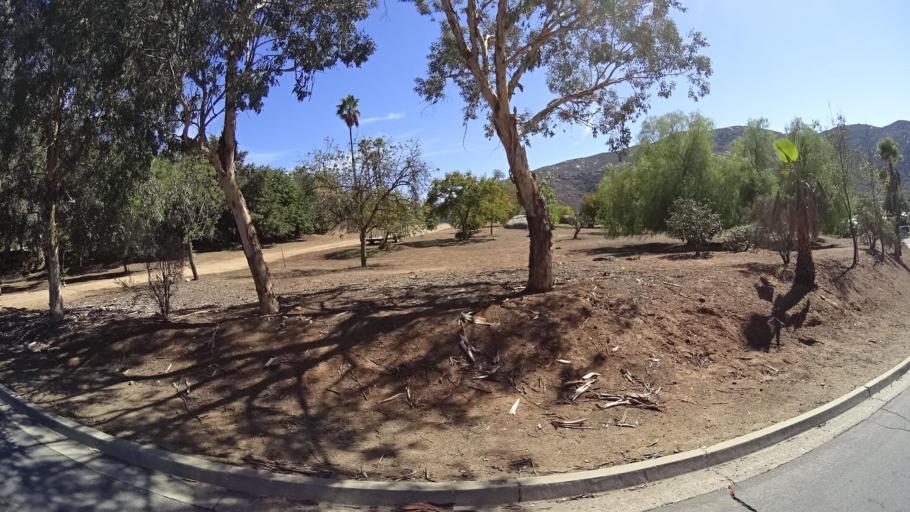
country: US
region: California
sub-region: San Diego County
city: Harbison Canyon
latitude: 32.8617
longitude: -116.8418
